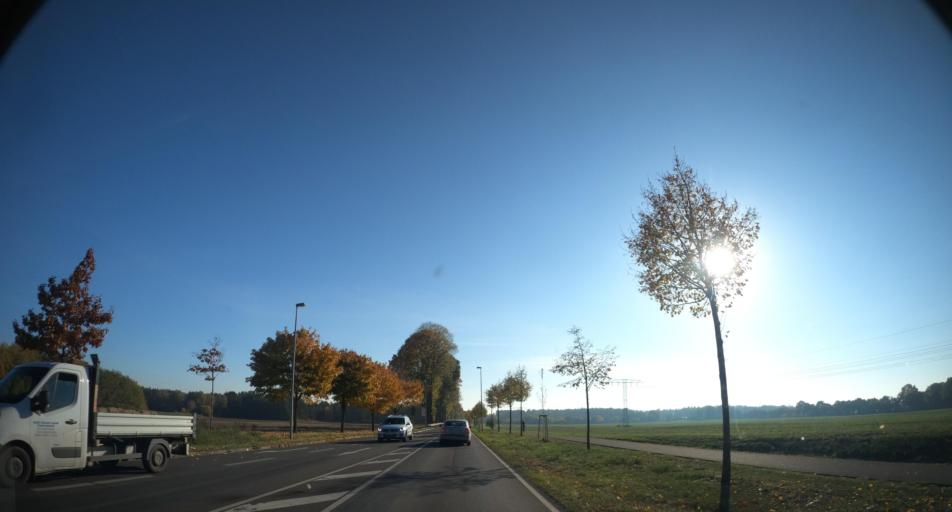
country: DE
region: Mecklenburg-Vorpommern
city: Ueckermunde
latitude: 53.7207
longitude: 14.0629
